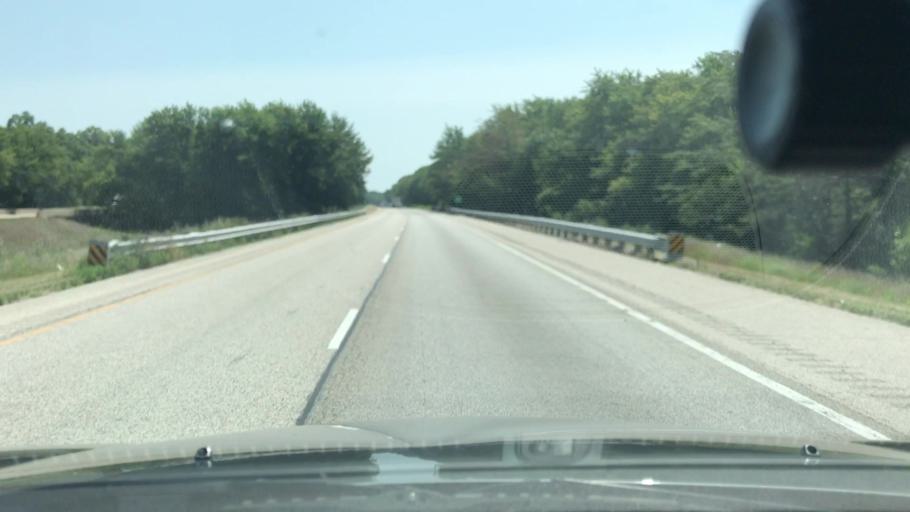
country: US
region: Illinois
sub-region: Washington County
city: Nashville
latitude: 38.4110
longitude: -89.4284
